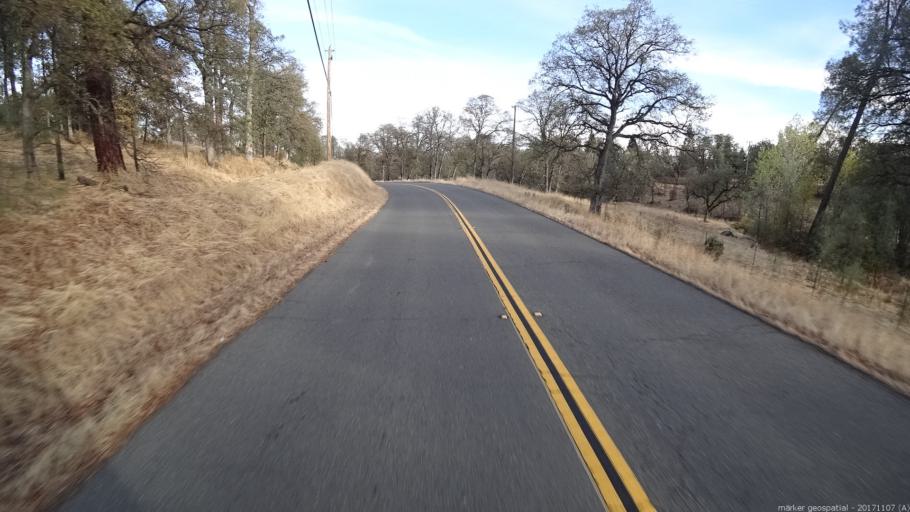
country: US
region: California
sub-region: Shasta County
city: Shasta
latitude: 40.5177
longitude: -122.4747
